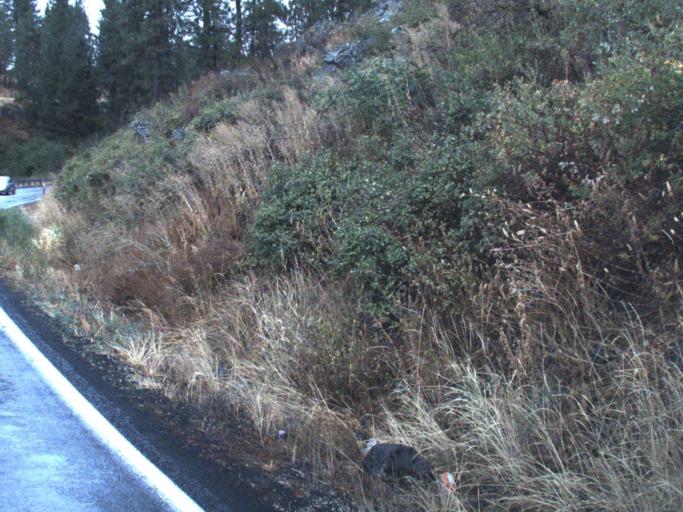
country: US
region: Washington
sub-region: Spokane County
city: Medical Lake
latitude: 47.7341
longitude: -117.8729
